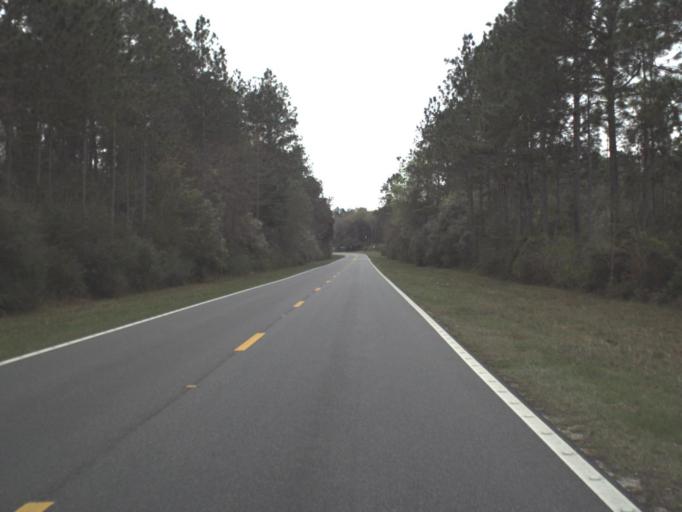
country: US
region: Florida
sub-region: Gulf County
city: Wewahitchka
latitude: 30.0331
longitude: -84.9836
